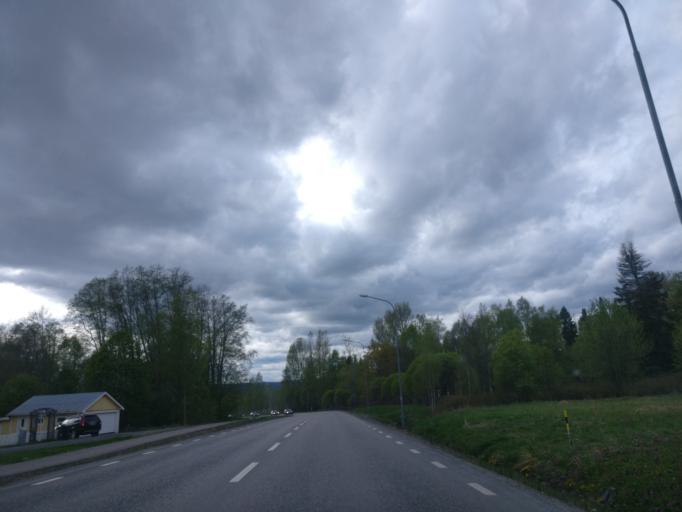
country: SE
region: Vaesternorrland
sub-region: Timra Kommun
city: Soraker
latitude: 62.5074
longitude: 17.5025
